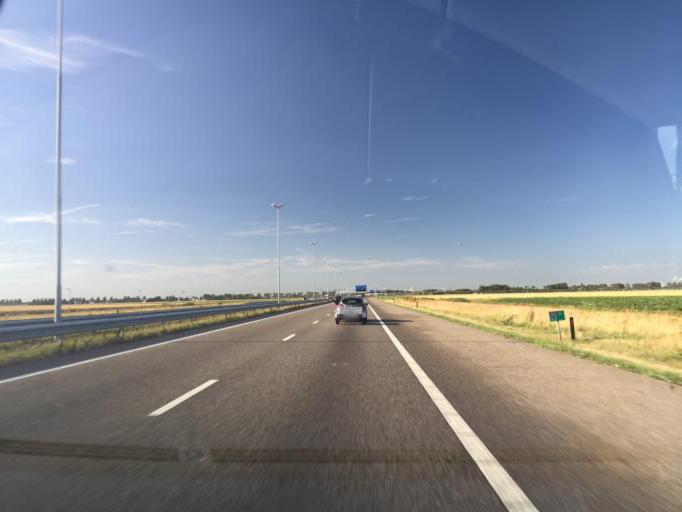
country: NL
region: North Holland
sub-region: Gemeente Haarlemmermeer
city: Hoofddorp
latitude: 52.3409
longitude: 4.7352
